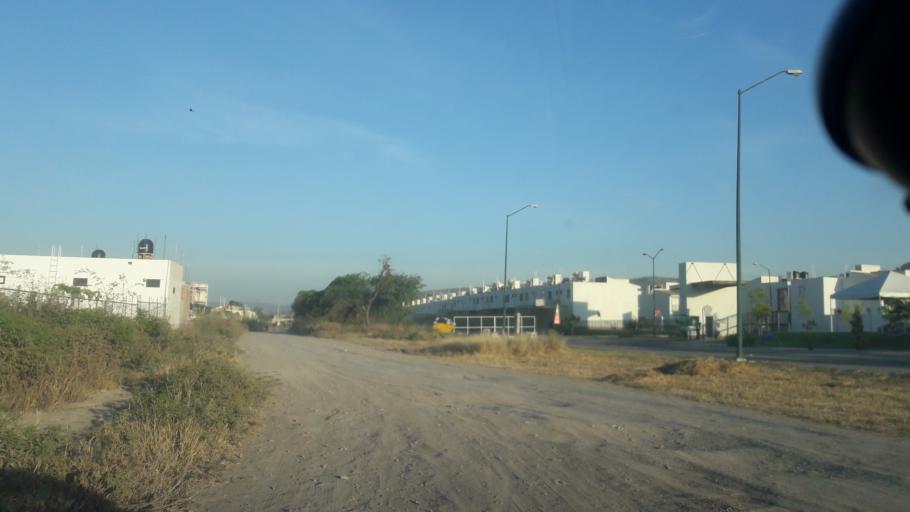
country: MX
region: Guanajuato
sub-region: Leon
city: Medina
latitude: 21.1643
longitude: -101.6339
